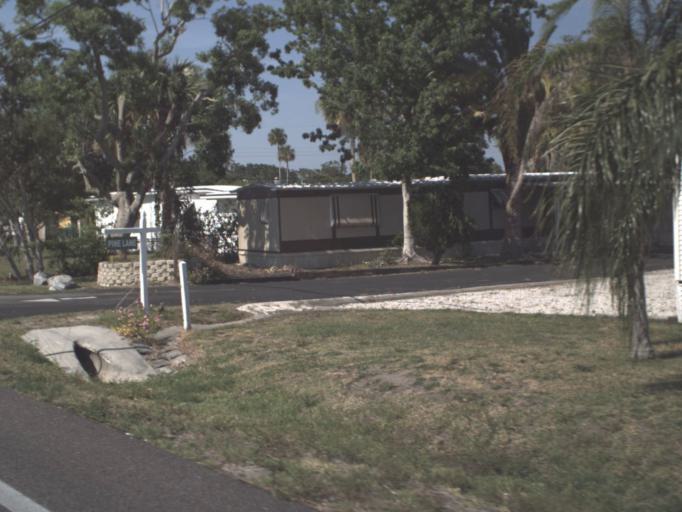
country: US
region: Florida
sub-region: Brevard County
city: Port Saint John
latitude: 28.5063
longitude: -80.7844
